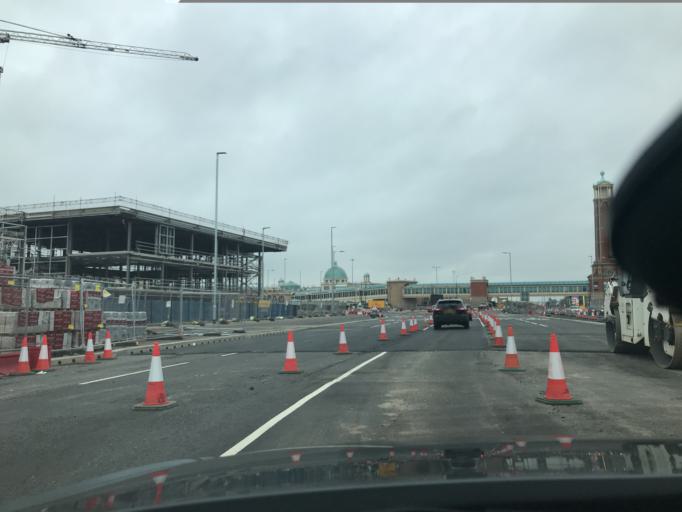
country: GB
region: England
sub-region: City and Borough of Salford
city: Eccles
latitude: 53.4645
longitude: -2.3394
